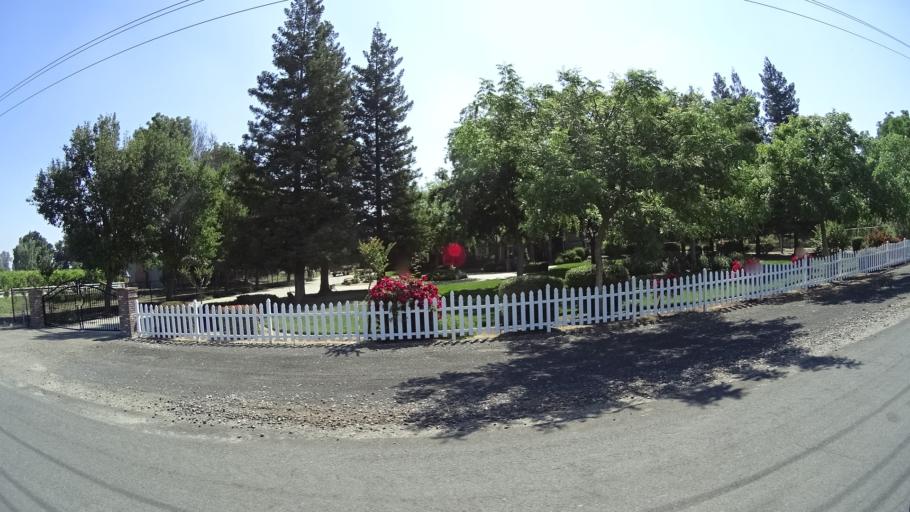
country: US
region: California
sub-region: Fresno County
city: Kingsburg
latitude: 36.4760
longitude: -119.5508
